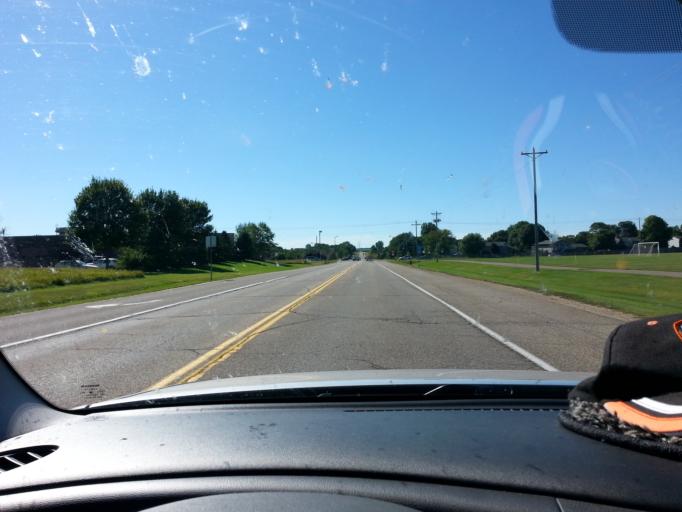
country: US
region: Minnesota
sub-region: Dakota County
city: Farmington
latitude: 44.6669
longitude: -93.1742
